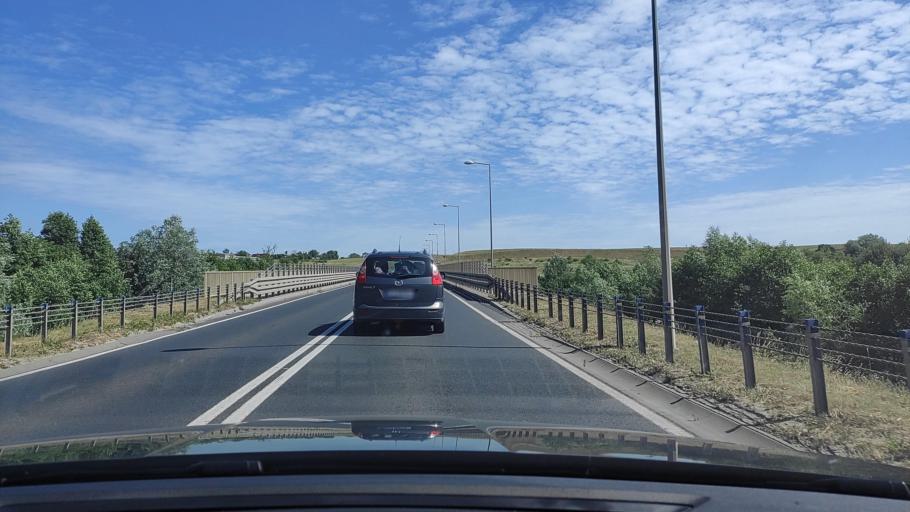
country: PL
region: Greater Poland Voivodeship
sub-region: Powiat poznanski
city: Murowana Goslina
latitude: 52.5796
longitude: 16.9814
